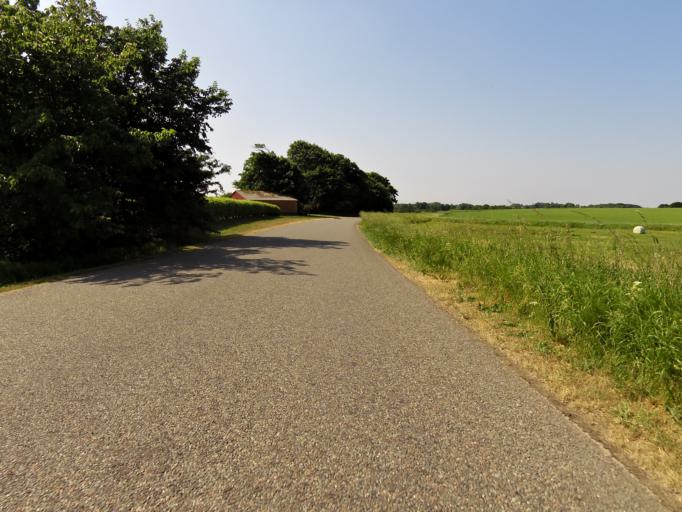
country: DK
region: Central Jutland
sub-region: Holstebro Kommune
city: Vinderup
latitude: 56.4789
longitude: 8.8277
